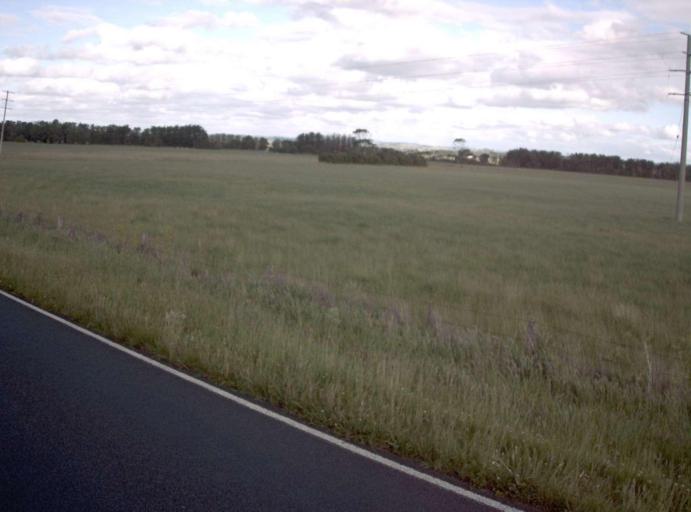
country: AU
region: Victoria
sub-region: Bass Coast
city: North Wonthaggi
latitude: -38.5337
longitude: 145.8736
